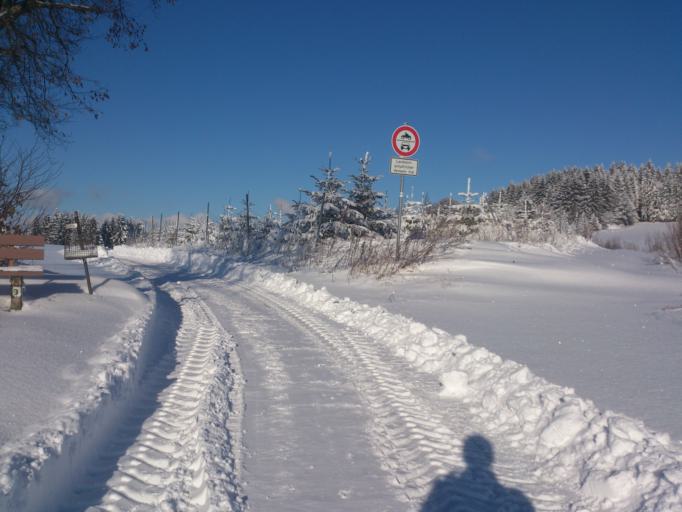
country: DE
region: Bavaria
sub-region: Upper Franconia
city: Rugendorf
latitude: 50.1959
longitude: 11.4980
